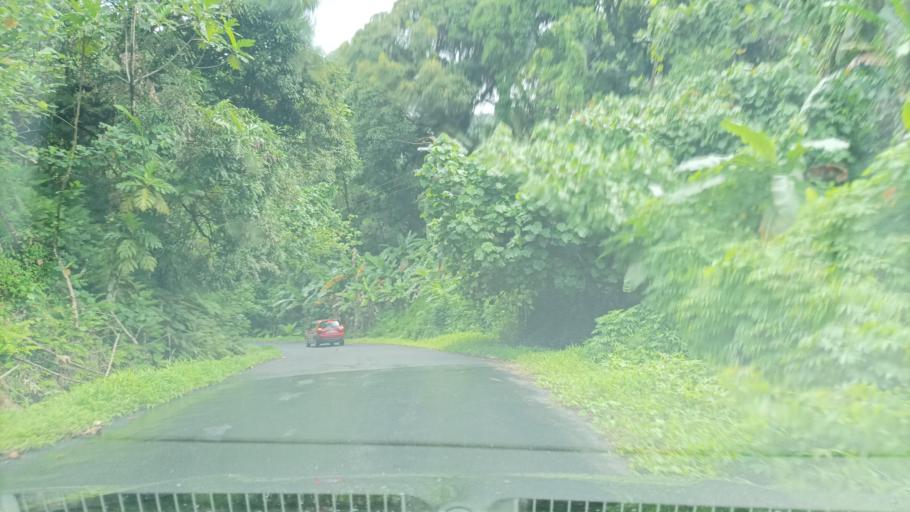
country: FM
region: Pohnpei
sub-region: Madolenihm Municipality
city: Madolenihm Municipality Government
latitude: 6.9192
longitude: 158.3112
